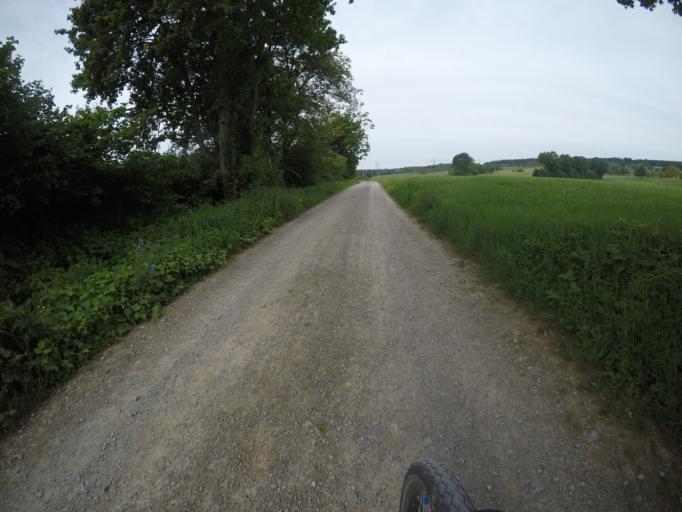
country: DE
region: Baden-Wuerttemberg
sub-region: Tuebingen Region
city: Pliezhausen
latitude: 48.5870
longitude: 9.1624
